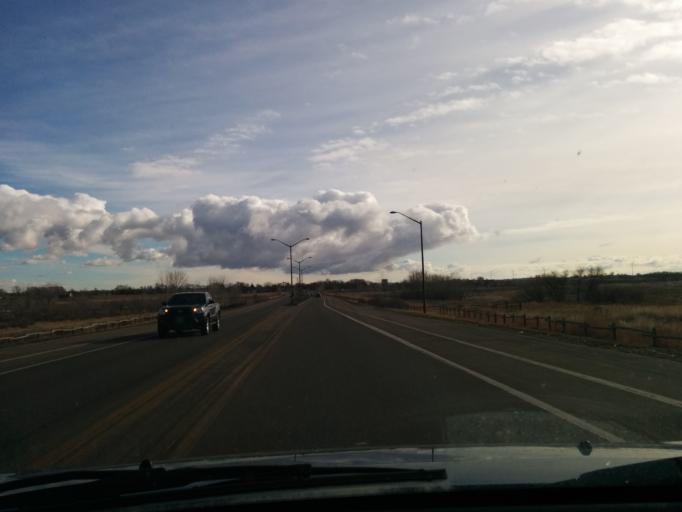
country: US
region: Colorado
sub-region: Larimer County
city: Fort Collins
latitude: 40.5670
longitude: -105.0263
